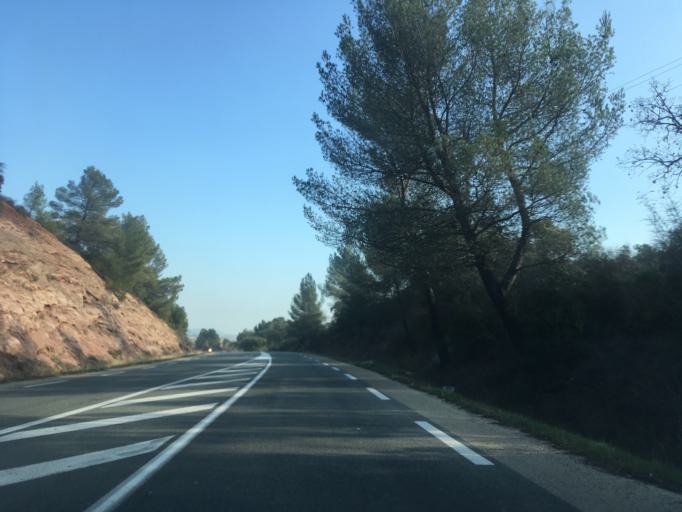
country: FR
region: Provence-Alpes-Cote d'Azur
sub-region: Departement du Var
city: Vidauban
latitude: 43.4354
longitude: 6.4438
